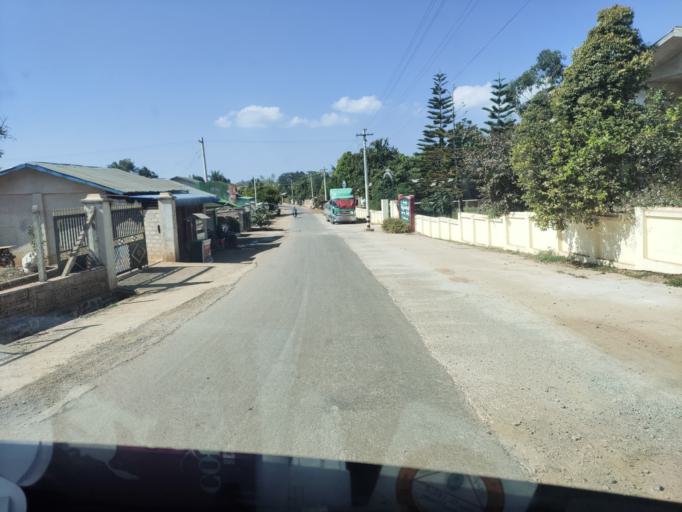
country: MM
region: Mandalay
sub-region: Pyin Oo Lwin District
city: Pyin Oo Lwin
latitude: 21.9529
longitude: 96.3947
